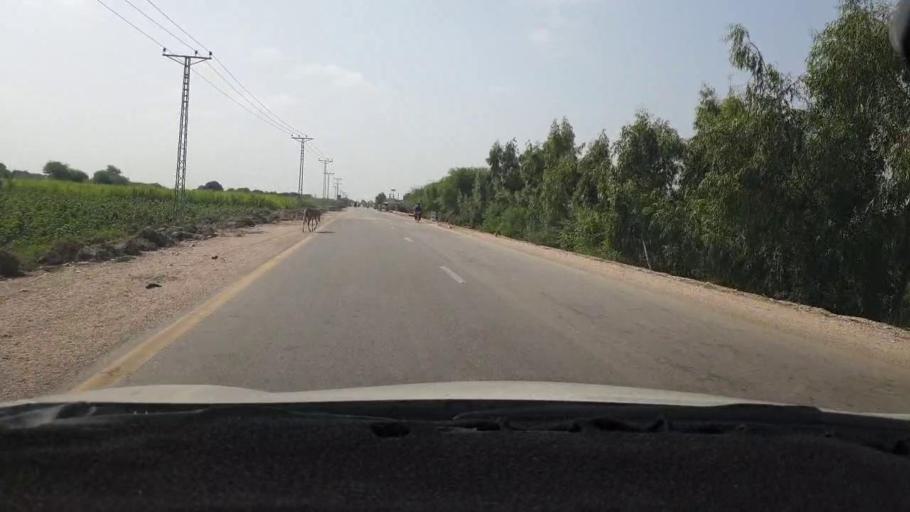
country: PK
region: Sindh
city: Mirpur Khas
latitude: 25.7737
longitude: 69.0713
